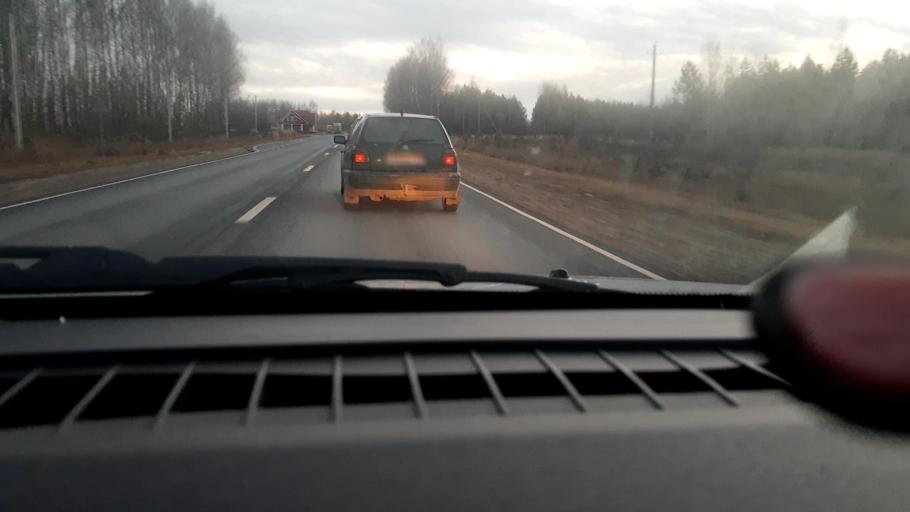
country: RU
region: Nizjnij Novgorod
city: Krasnyye Baki
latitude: 57.0189
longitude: 45.1169
